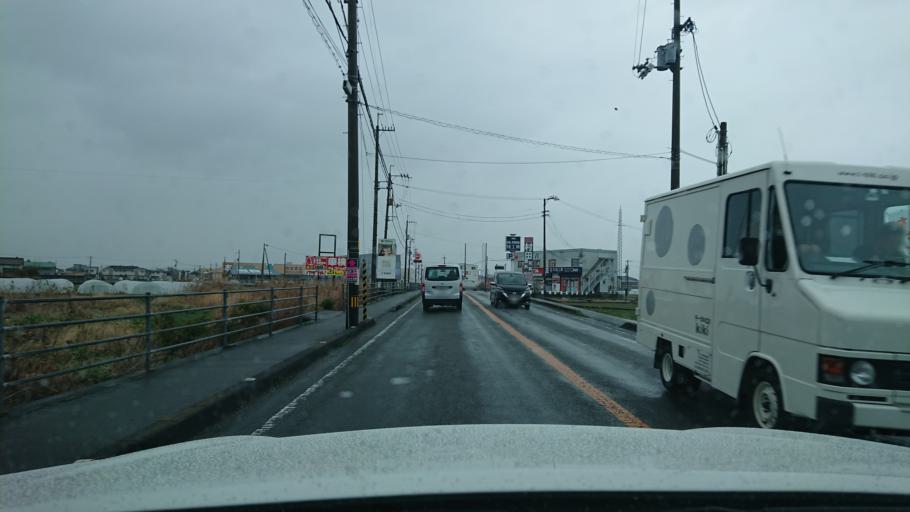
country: JP
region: Tokushima
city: Ishii
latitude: 34.0861
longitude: 134.4919
